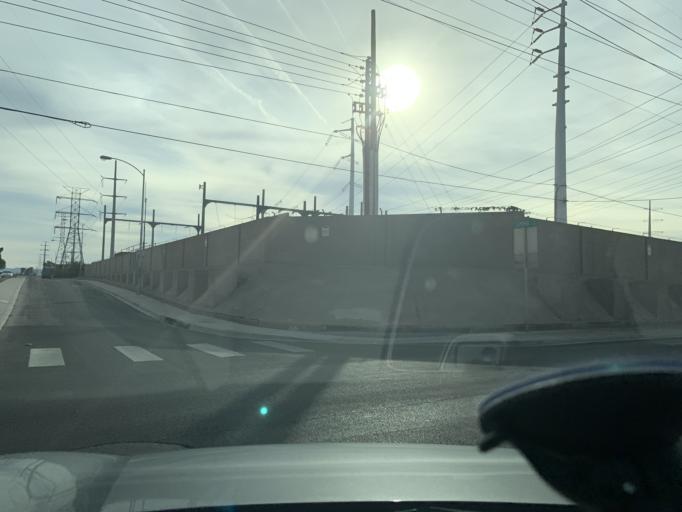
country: US
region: Nevada
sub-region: Clark County
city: Spring Valley
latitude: 36.1152
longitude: -115.2123
